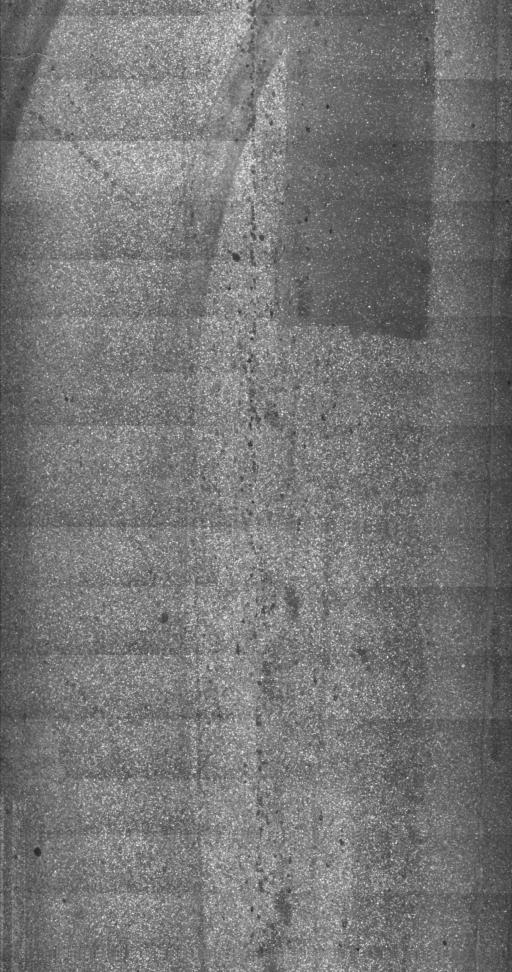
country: US
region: Vermont
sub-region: Lamoille County
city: Morristown
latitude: 44.4653
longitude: -72.6846
